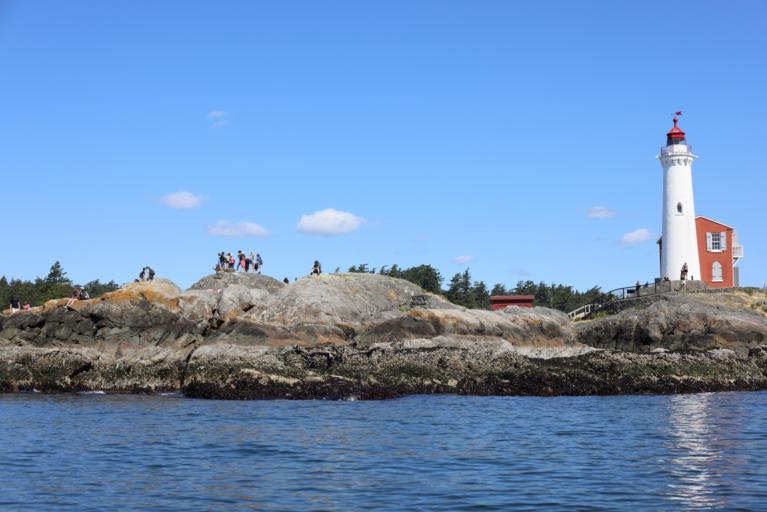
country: CA
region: British Columbia
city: Colwood
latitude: 48.4294
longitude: -123.4472
